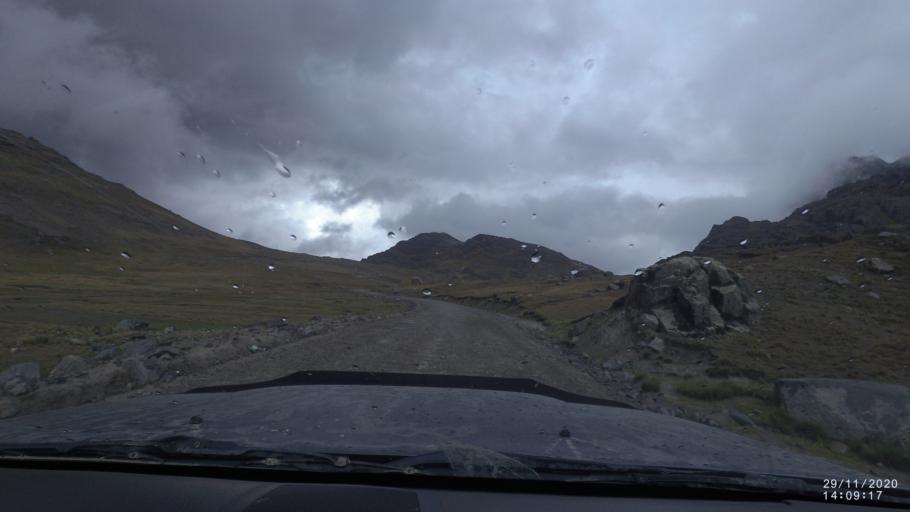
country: BO
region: Cochabamba
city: Sipe Sipe
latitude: -17.2263
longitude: -66.3848
